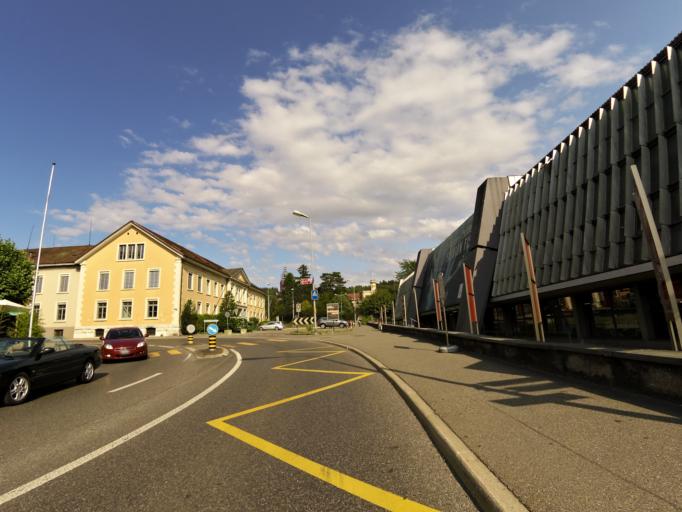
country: CH
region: Solothurn
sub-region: Bezirk Olten
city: Schonenwerd
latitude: 47.3723
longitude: 7.9992
